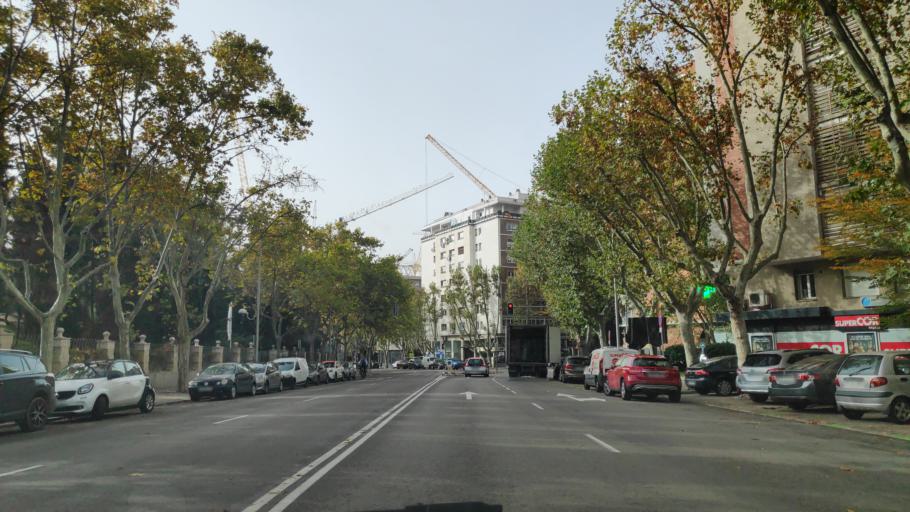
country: ES
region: Madrid
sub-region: Provincia de Madrid
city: Chamartin
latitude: 40.4567
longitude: -3.6863
